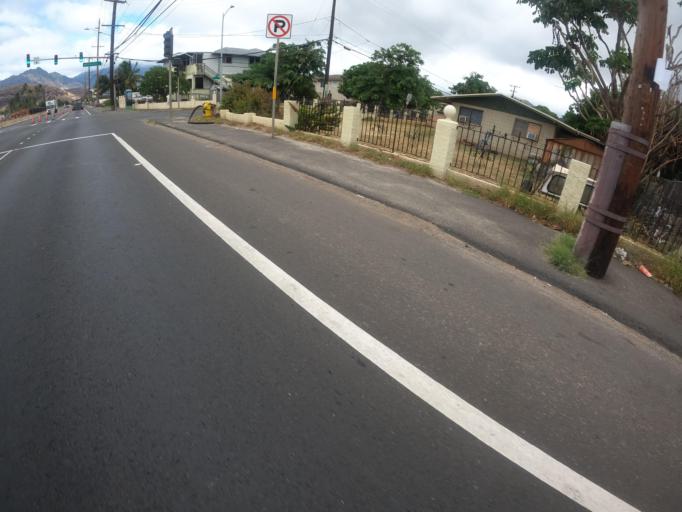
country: US
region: Hawaii
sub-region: Honolulu County
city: Ma'ili
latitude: 21.4082
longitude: -158.1772
